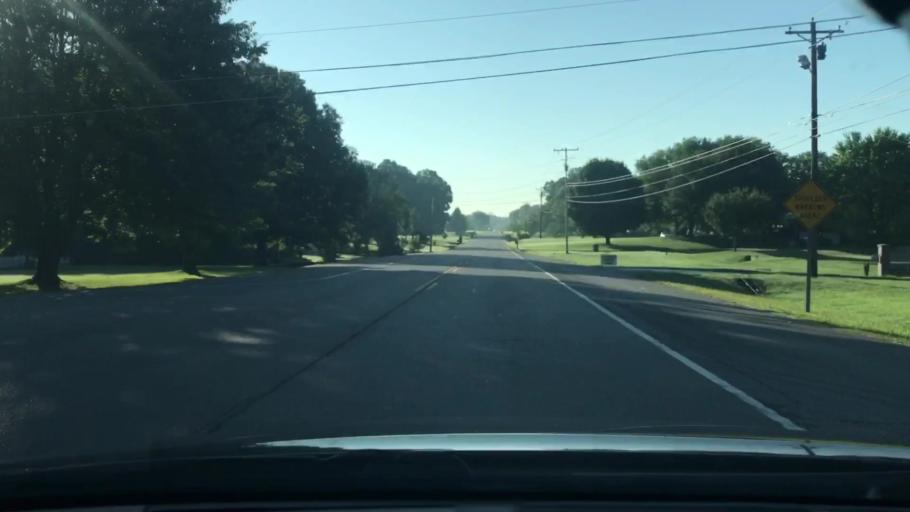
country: US
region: Tennessee
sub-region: Sumner County
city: Millersville
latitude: 36.4126
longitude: -86.7082
